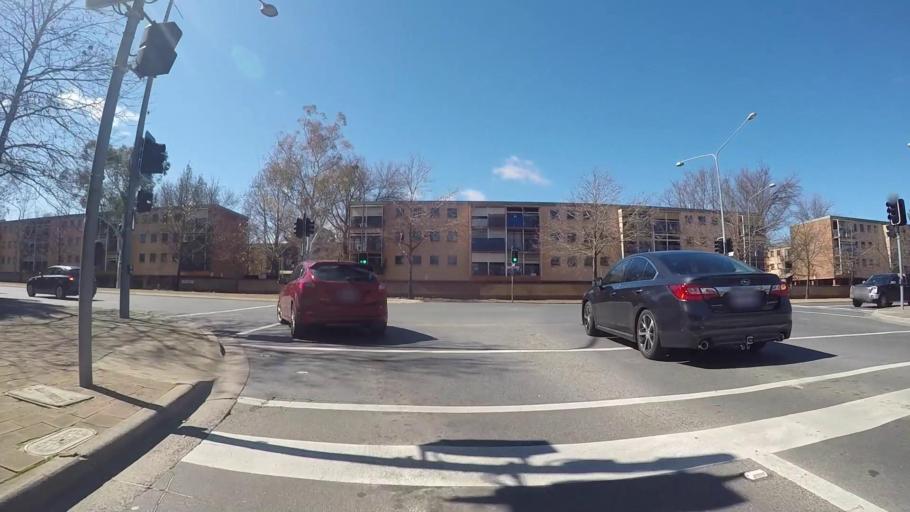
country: AU
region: Australian Capital Territory
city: Canberra
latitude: -35.2804
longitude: 149.1358
